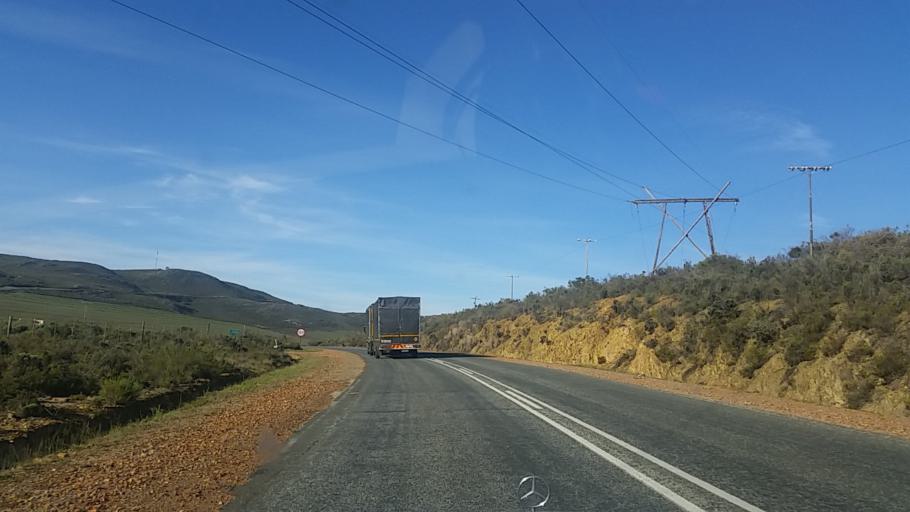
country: ZA
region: Western Cape
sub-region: Eden District Municipality
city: Knysna
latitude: -33.7400
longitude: 23.0377
